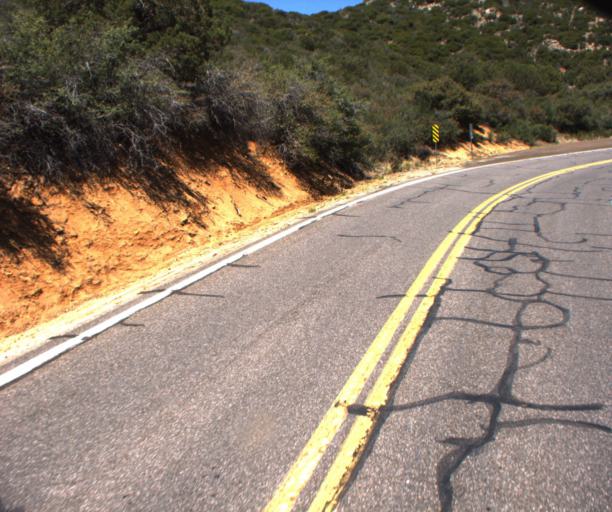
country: US
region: Arizona
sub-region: Yavapai County
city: Prescott
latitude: 34.4265
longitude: -112.5544
